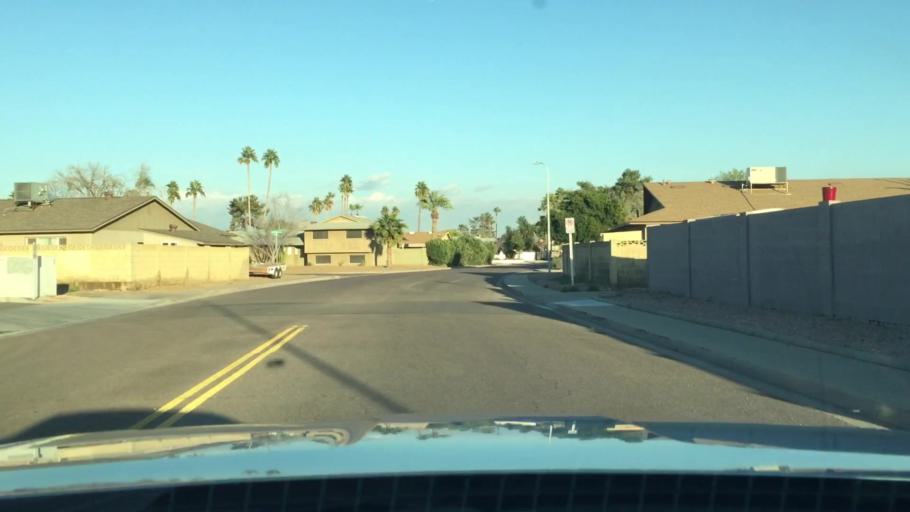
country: US
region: Arizona
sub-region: Maricopa County
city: Tempe
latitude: 33.3837
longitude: -111.9153
